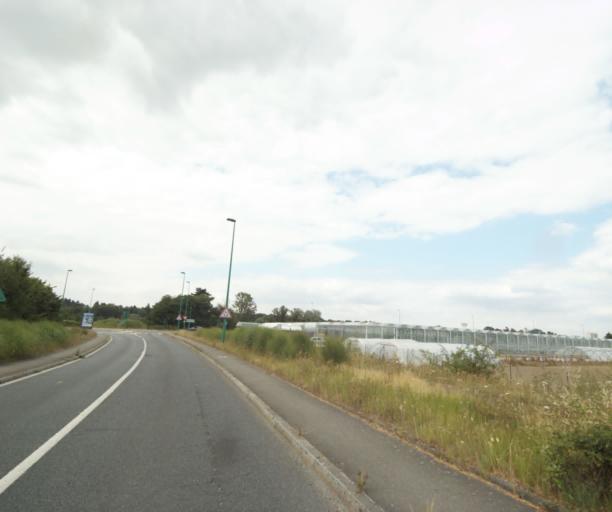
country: FR
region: Centre
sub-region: Departement du Loiret
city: Saint-Pryve-Saint-Mesmin
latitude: 47.8900
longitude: 1.8630
